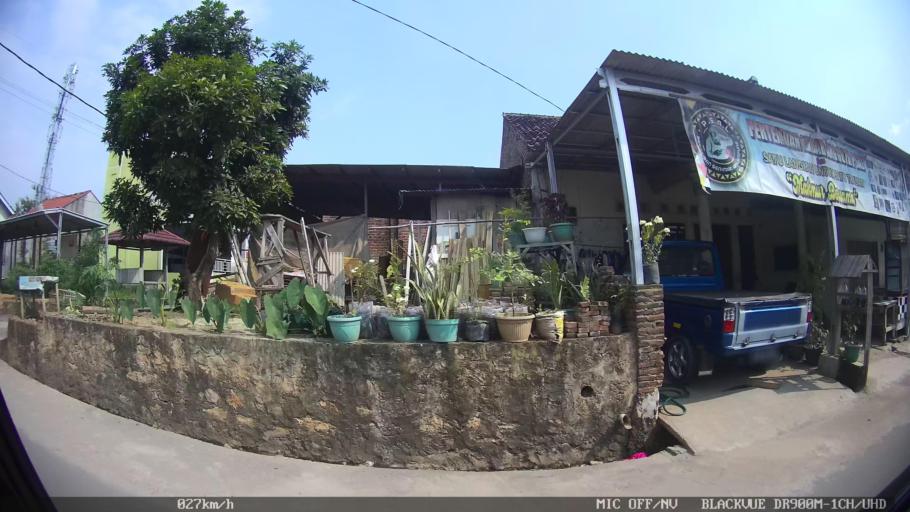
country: ID
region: Lampung
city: Natar
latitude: -5.3477
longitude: 105.2210
